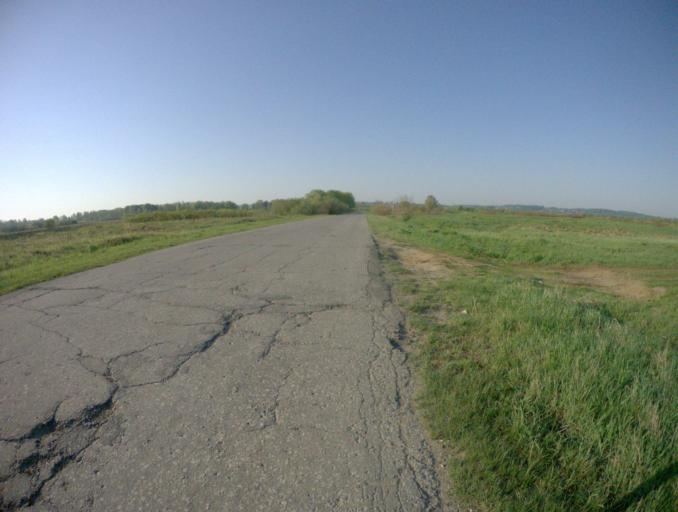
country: RU
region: Vladimir
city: Vyazniki
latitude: 56.2663
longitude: 42.1714
